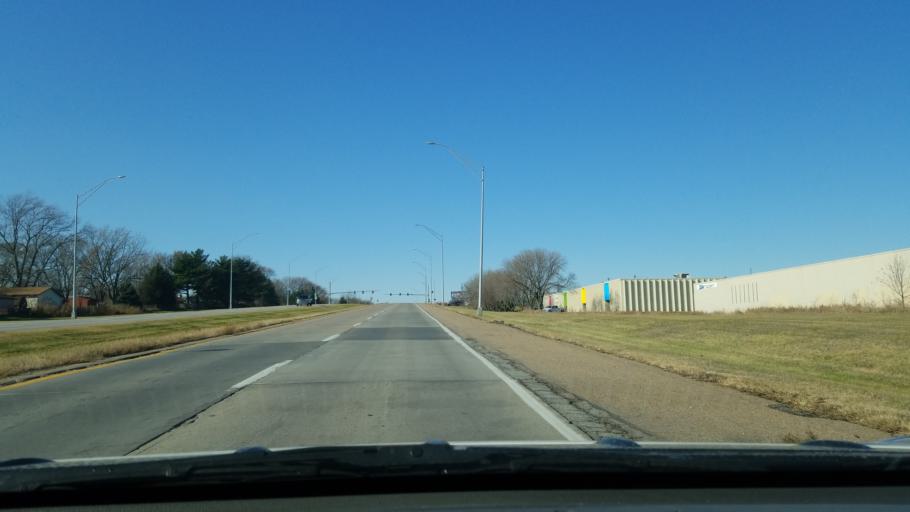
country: US
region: Nebraska
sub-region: Douglas County
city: Ralston
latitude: 41.2126
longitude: -96.0679
